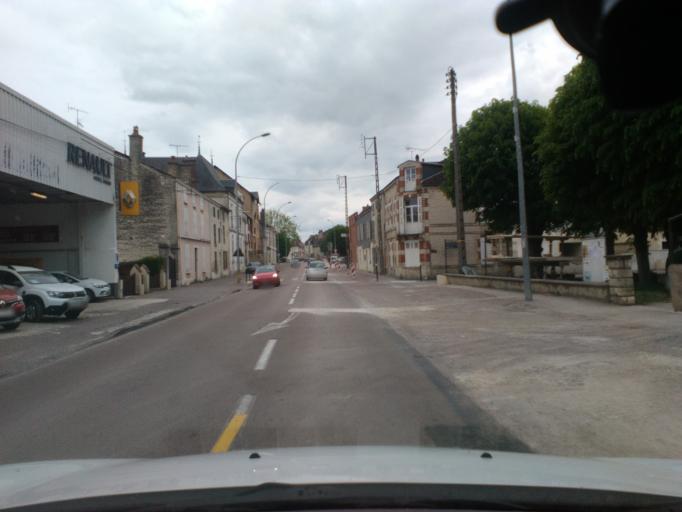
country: FR
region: Champagne-Ardenne
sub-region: Departement de l'Aube
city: Bar-sur-Aube
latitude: 48.2364
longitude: 4.7023
